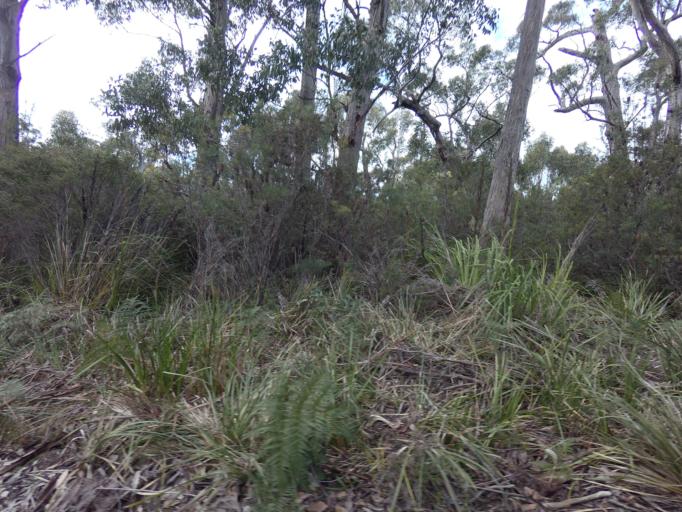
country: AU
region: Tasmania
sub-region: Huon Valley
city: Geeveston
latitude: -43.4807
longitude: 146.9365
